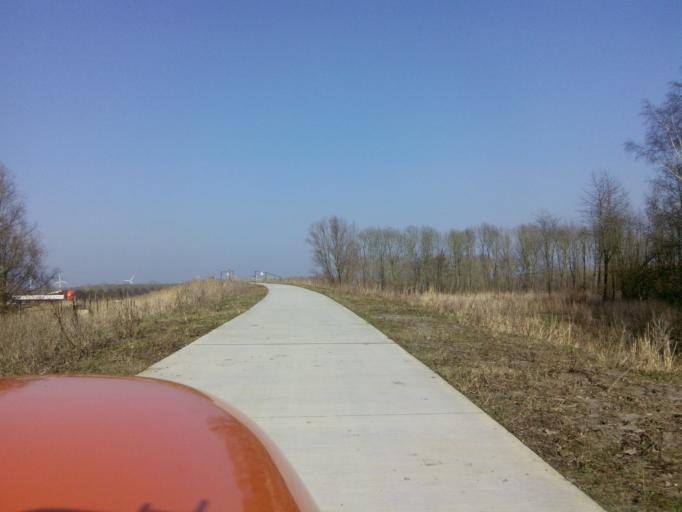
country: NL
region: Flevoland
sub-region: Gemeente Zeewolde
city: Zeewolde
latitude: 52.3235
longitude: 5.4487
